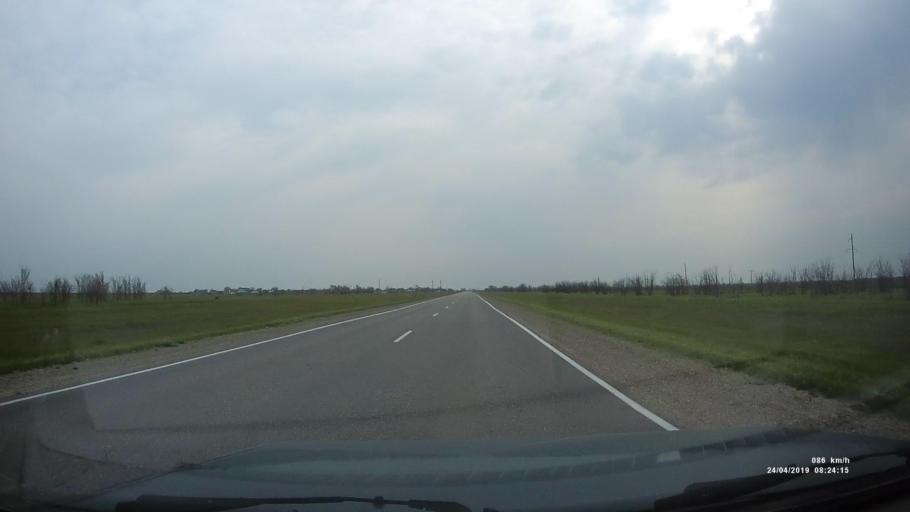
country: RU
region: Kalmykiya
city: Priyutnoye
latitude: 46.1200
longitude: 43.7513
